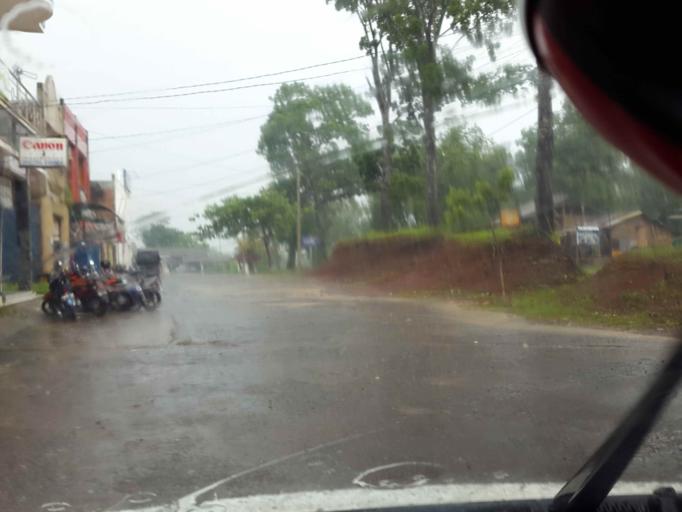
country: ID
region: West Java
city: Cilandak
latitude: -6.9794
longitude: 106.7161
